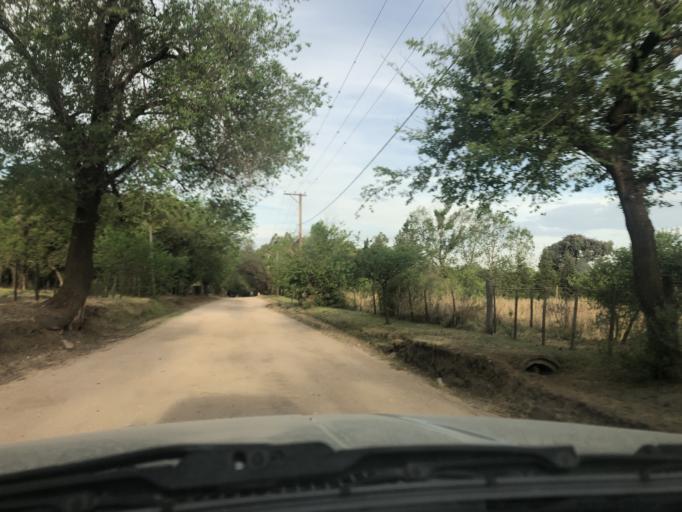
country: AR
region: Cordoba
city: La Granja
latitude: -31.0177
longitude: -64.2412
